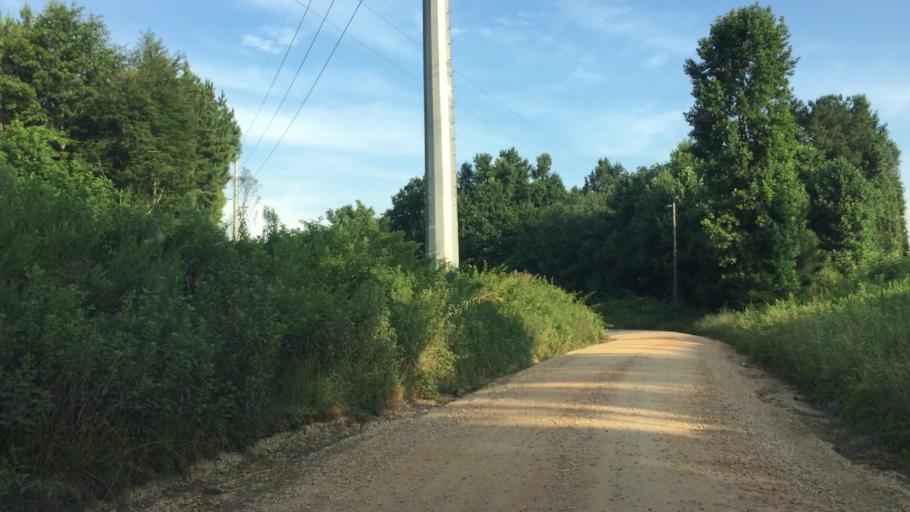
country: US
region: Georgia
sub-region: Henry County
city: McDonough
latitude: 33.5287
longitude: -84.1277
